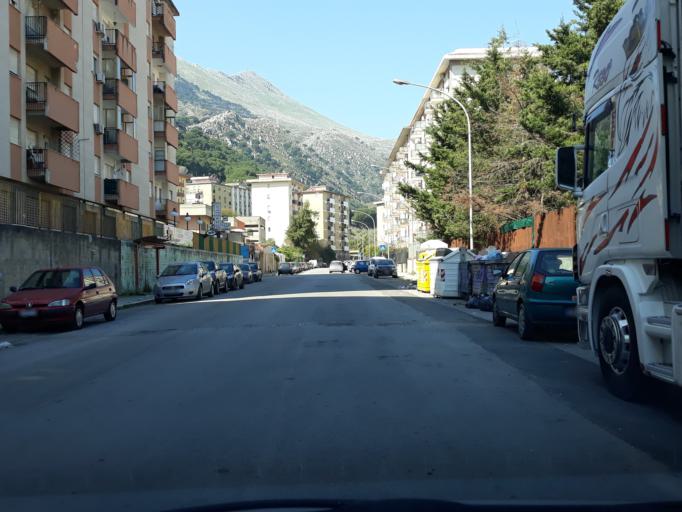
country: IT
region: Sicily
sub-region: Palermo
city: Piano dei Geli
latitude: 38.1248
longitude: 13.2953
